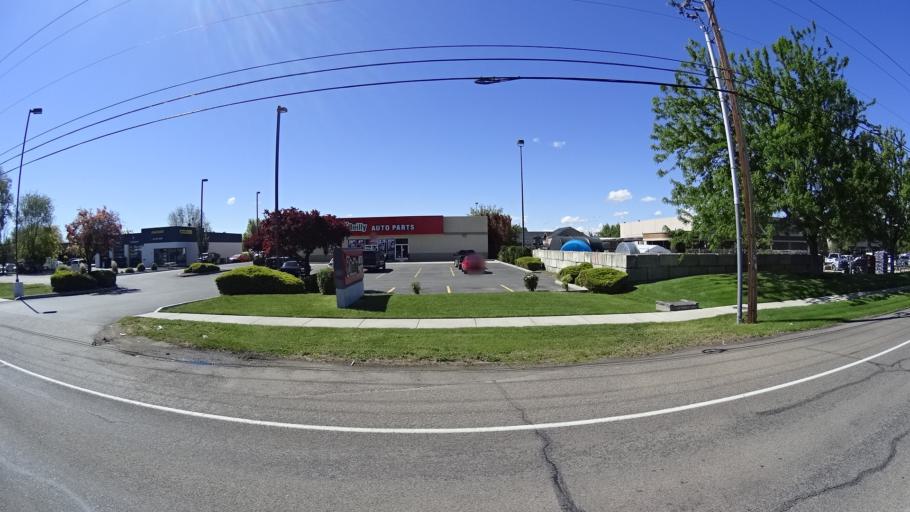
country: US
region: Idaho
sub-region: Ada County
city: Meridian
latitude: 43.6194
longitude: -116.3708
